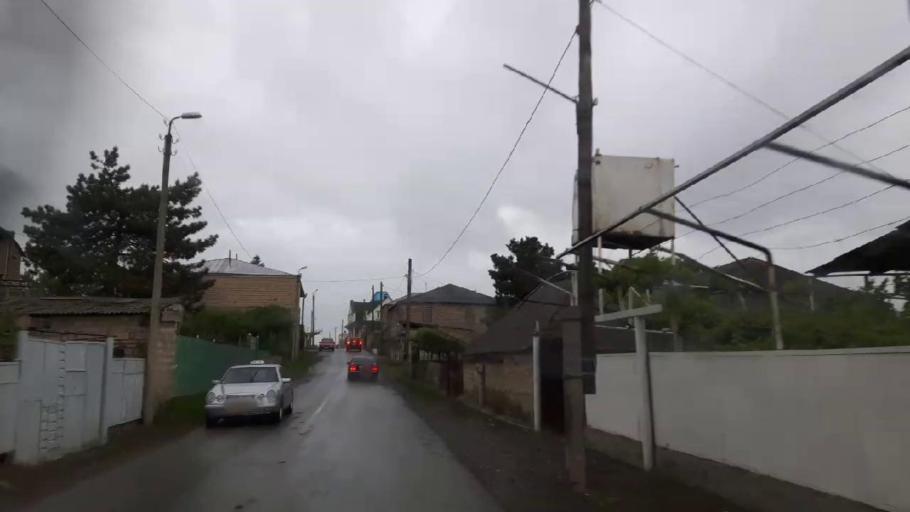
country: GE
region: Shida Kartli
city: Gori
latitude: 41.9884
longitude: 44.0110
